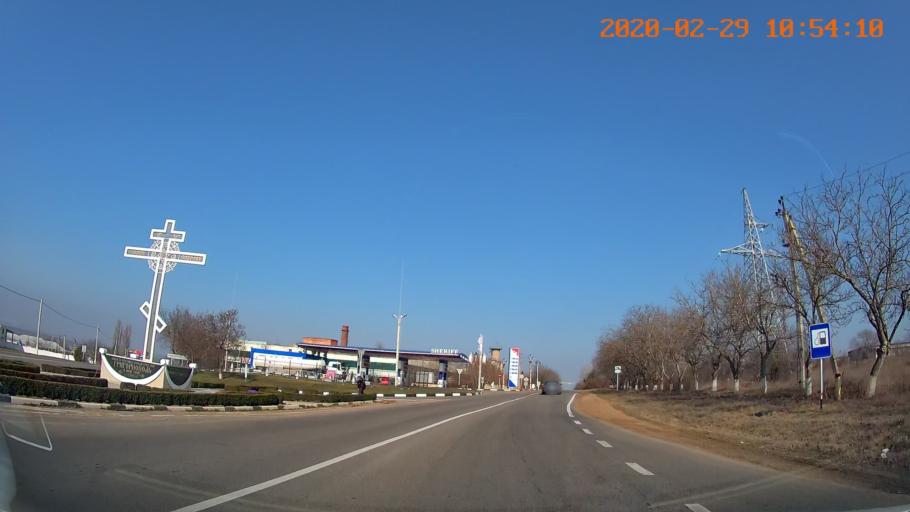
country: MD
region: Telenesti
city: Grigoriopol
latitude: 47.1205
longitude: 29.3279
